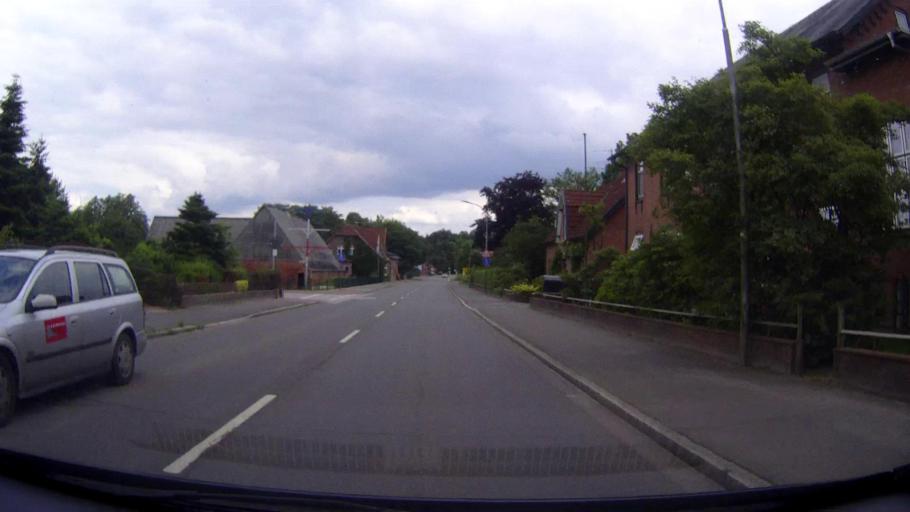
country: DE
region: Schleswig-Holstein
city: Gokels
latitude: 54.1205
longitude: 9.4415
